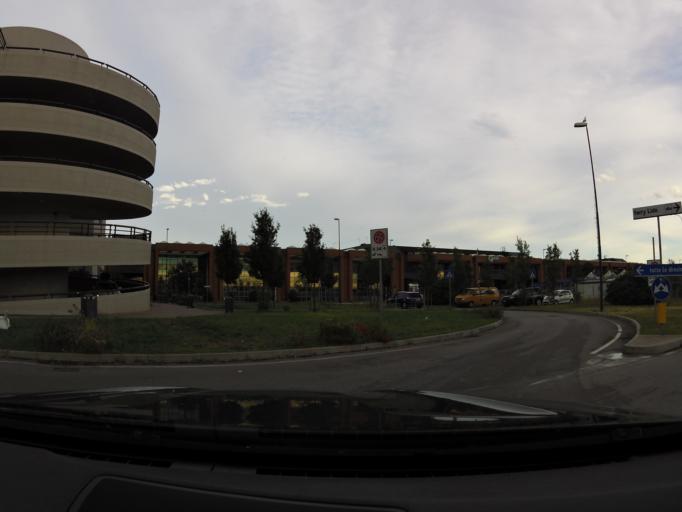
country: IT
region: Veneto
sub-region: Provincia di Venezia
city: Venice
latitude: 45.4417
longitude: 12.3052
